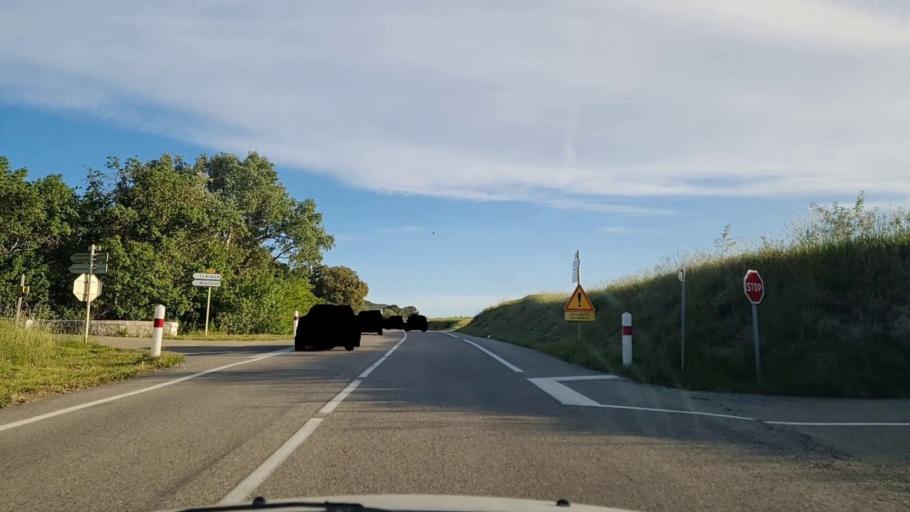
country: FR
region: Languedoc-Roussillon
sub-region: Departement du Gard
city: Ledignan
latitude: 43.9309
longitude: 4.1035
